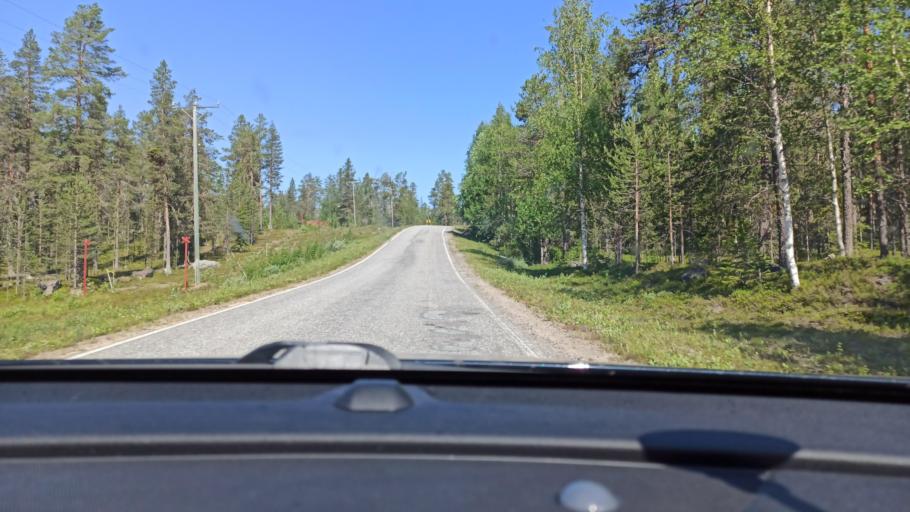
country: FI
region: Lapland
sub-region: Tunturi-Lappi
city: Kolari
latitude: 67.6359
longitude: 24.1578
